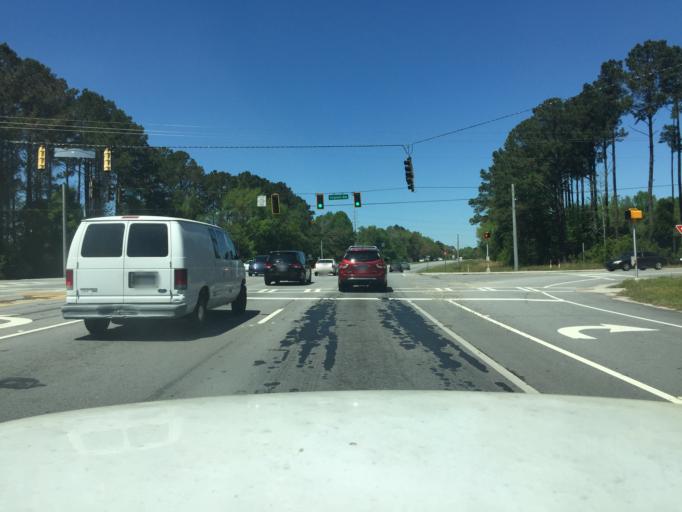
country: US
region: Georgia
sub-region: Chatham County
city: Montgomery
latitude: 31.9581
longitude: -81.0980
